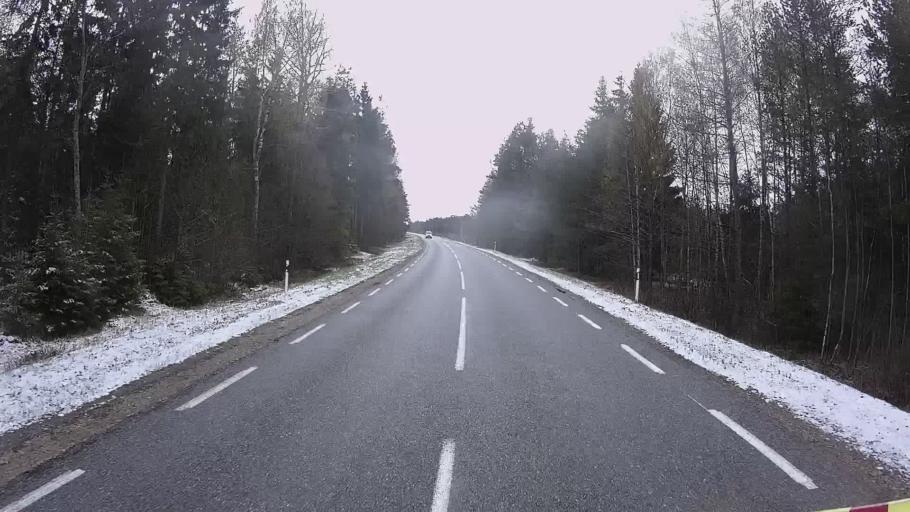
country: EE
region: Hiiumaa
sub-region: Kaerdla linn
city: Kardla
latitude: 59.0283
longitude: 22.6724
